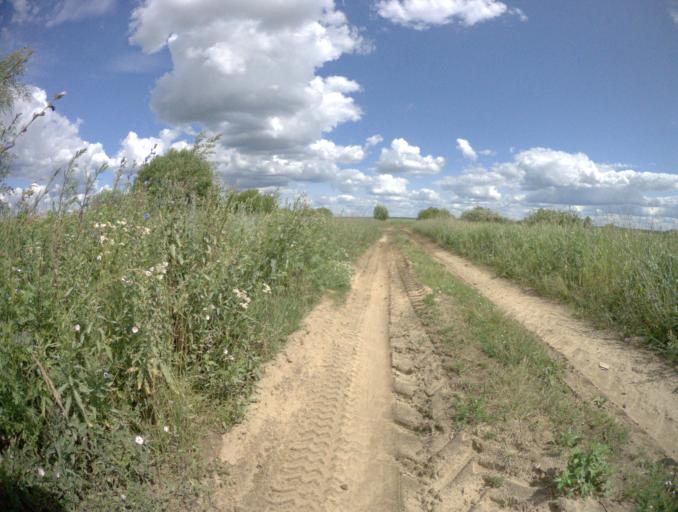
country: RU
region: Vladimir
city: Orgtrud
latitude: 56.3114
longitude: 40.6480
